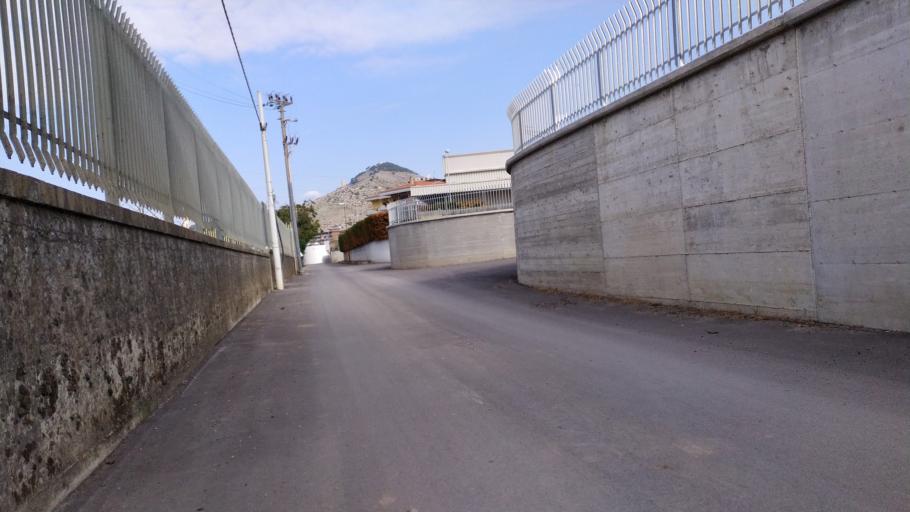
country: IT
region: Campania
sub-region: Provincia di Caserta
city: Maddaloni
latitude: 41.0278
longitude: 14.3970
